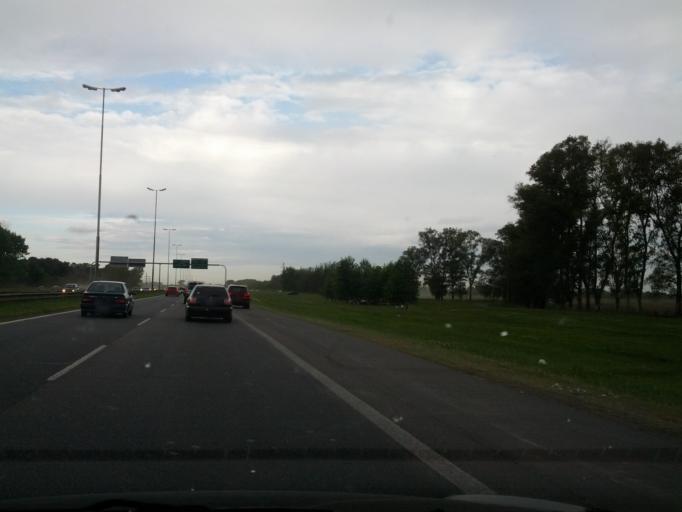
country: AR
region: Buenos Aires
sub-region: Partido de Lujan
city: Lujan
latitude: -34.5710
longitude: -59.0500
